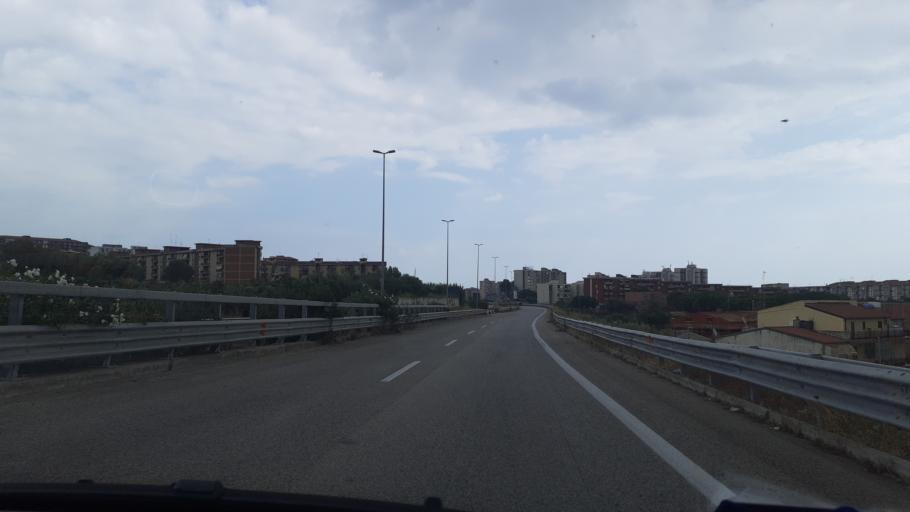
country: IT
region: Sicily
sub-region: Catania
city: Catania
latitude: 37.4775
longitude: 15.0445
